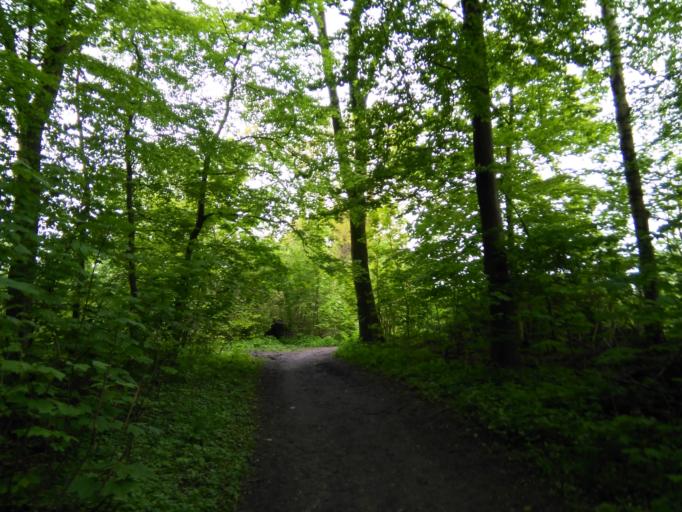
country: DK
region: Central Jutland
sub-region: Arhus Kommune
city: Arhus
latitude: 56.1219
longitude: 10.2006
